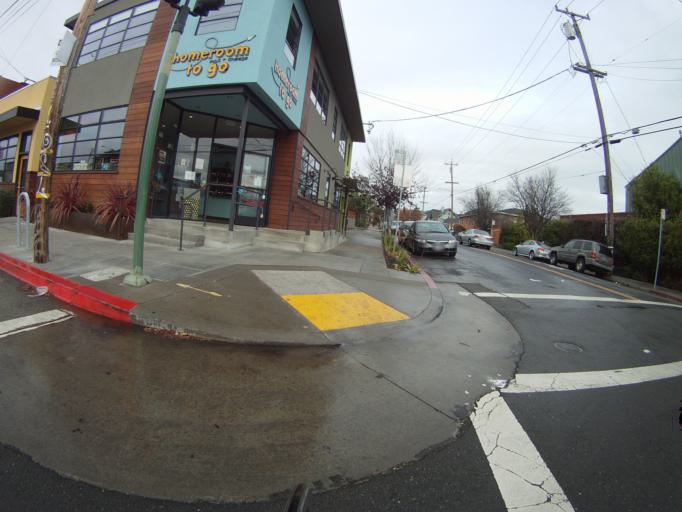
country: US
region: California
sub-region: Alameda County
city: Emeryville
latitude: 37.8287
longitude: -122.2609
